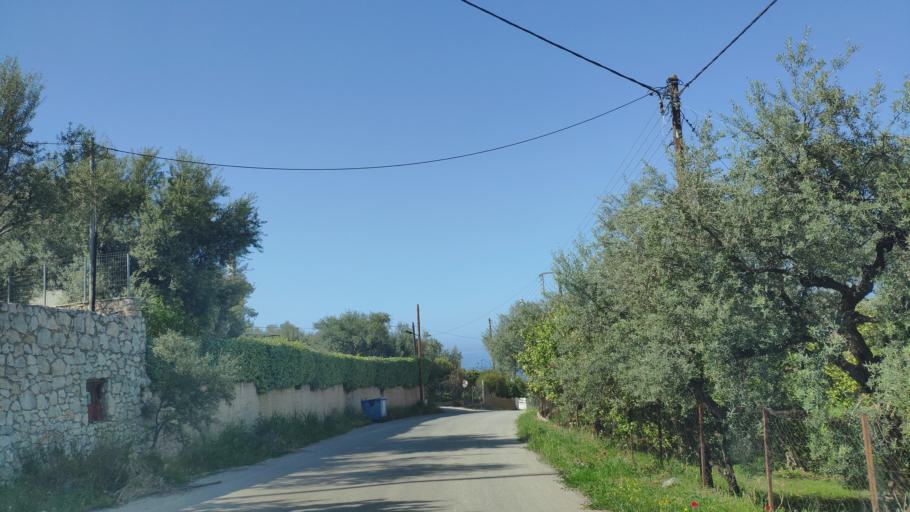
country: GR
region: West Greece
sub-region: Nomos Achaias
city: Aiyira
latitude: 38.1396
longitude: 22.3492
